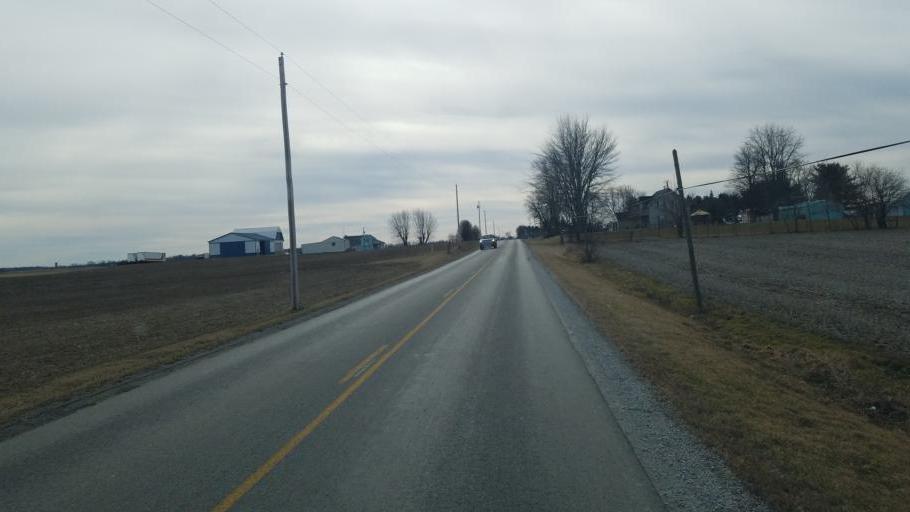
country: US
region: Ohio
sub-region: Hardin County
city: Kenton
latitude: 40.5586
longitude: -83.5112
